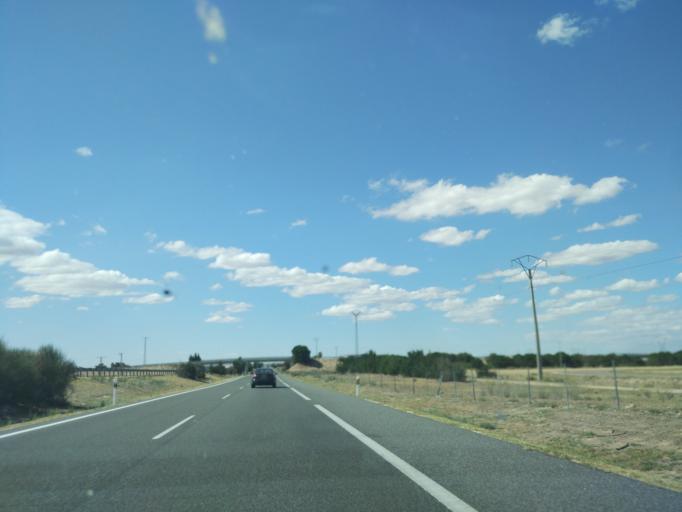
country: ES
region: Castille and Leon
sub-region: Provincia de Valladolid
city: San Vicente del Palacio
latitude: 41.2477
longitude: -4.8686
